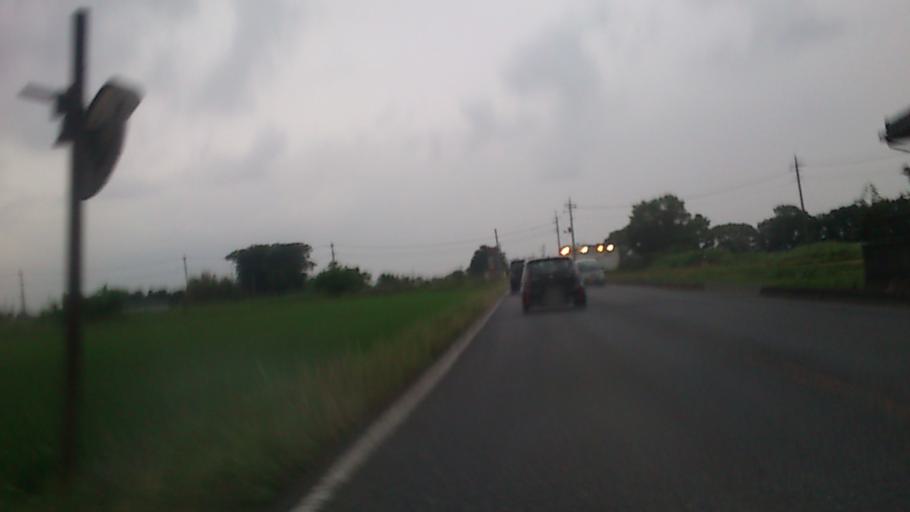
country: JP
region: Saitama
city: Kazo
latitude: 36.1585
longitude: 139.6100
